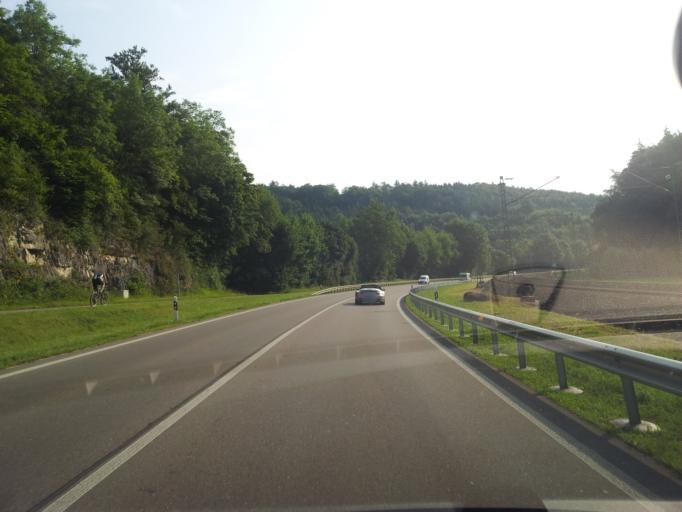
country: CH
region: Schaffhausen
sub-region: Bezirk Reiat
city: Stetten
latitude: 47.7349
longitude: 8.6794
